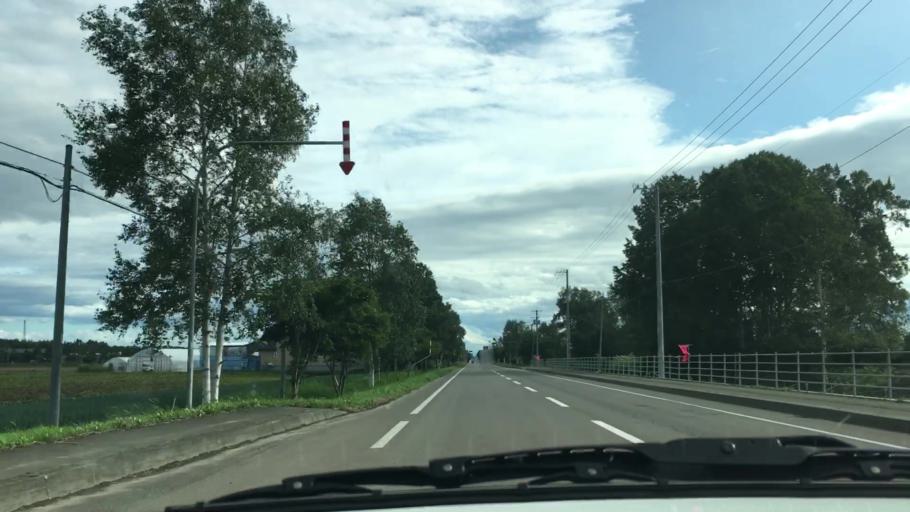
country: JP
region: Hokkaido
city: Otofuke
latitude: 43.2441
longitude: 143.2976
